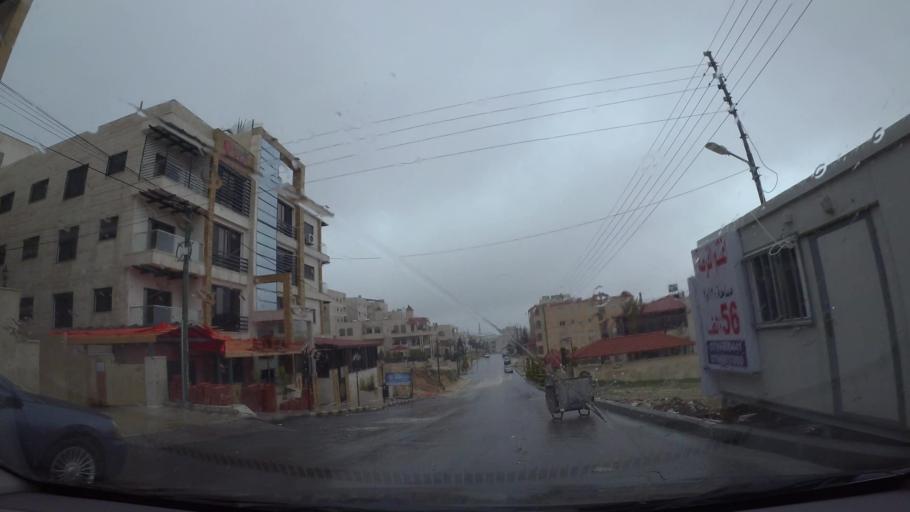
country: JO
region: Amman
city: Al Jubayhah
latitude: 32.0289
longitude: 35.8841
